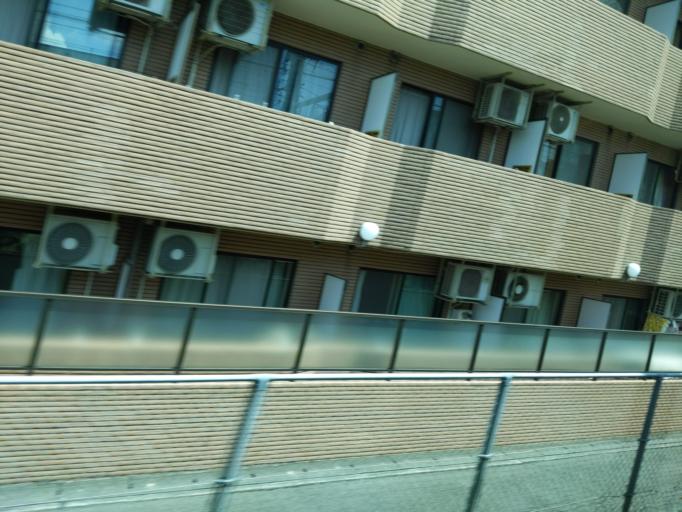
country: JP
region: Tokyo
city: Chofugaoka
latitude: 35.6249
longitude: 139.5605
